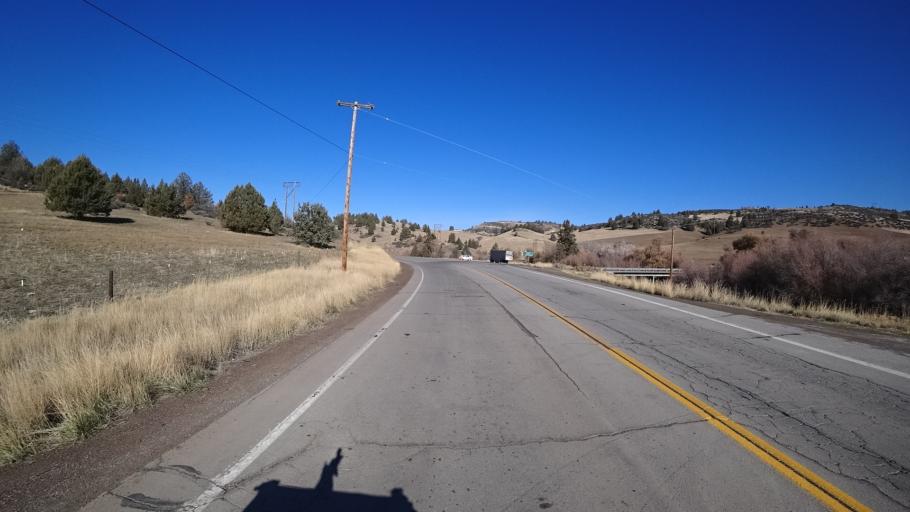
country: US
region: California
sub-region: Siskiyou County
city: Montague
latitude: 41.8648
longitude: -122.4644
